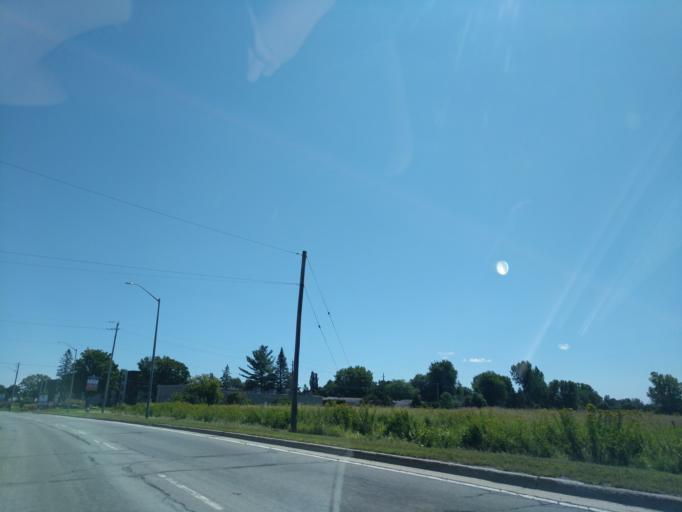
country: CA
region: Ontario
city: Bells Corners
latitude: 45.3524
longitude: -75.8421
